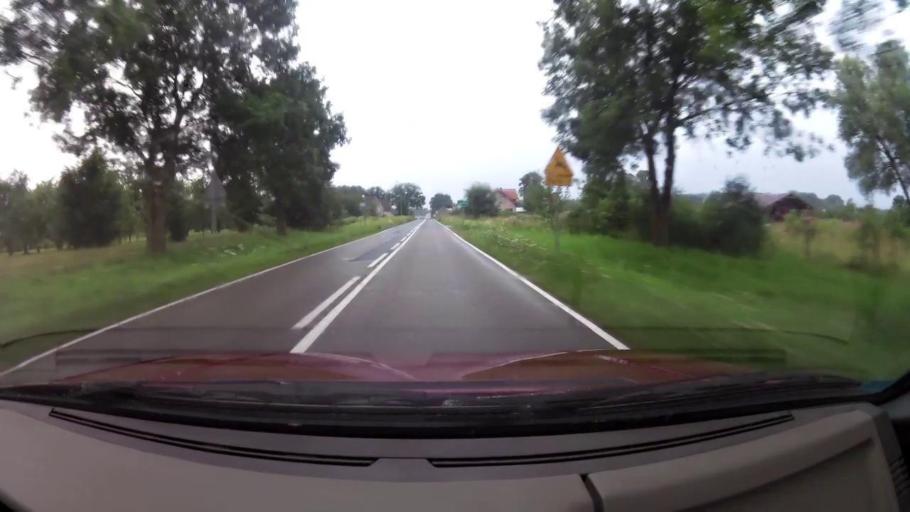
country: PL
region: West Pomeranian Voivodeship
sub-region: Powiat stargardzki
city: Stara Dabrowa
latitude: 53.3849
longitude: 15.1781
